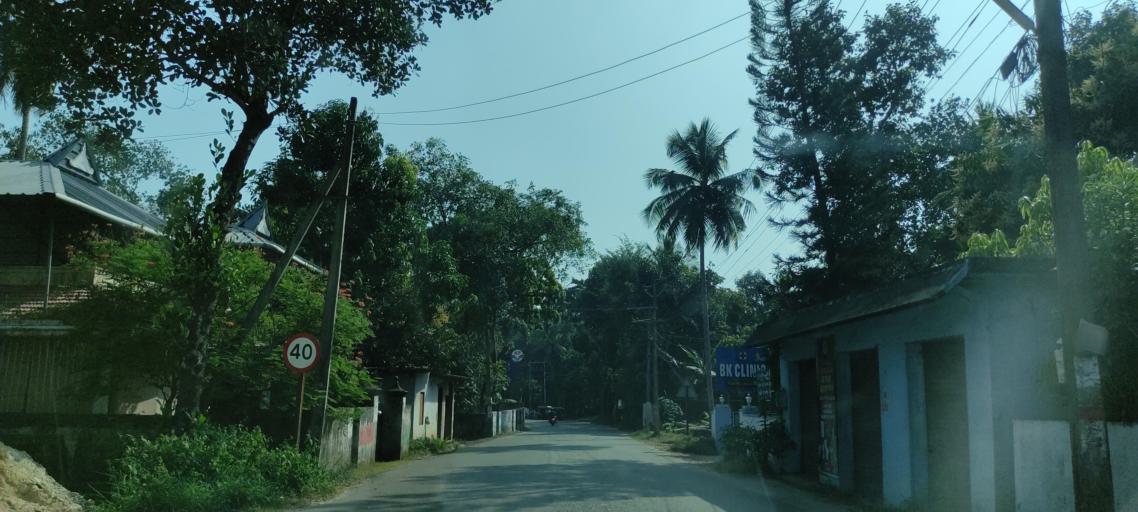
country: IN
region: Kerala
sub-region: Kollam
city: Panmana
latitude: 9.0468
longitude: 76.5755
